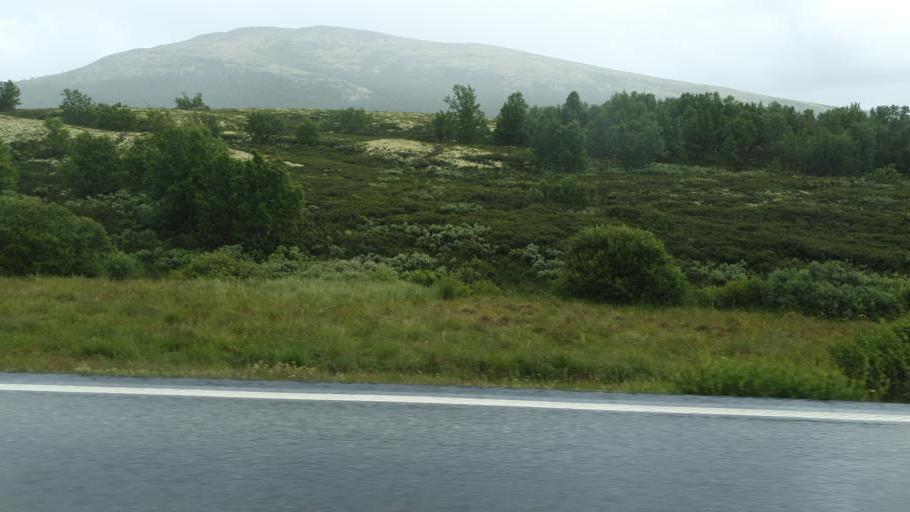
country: NO
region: Sor-Trondelag
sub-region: Oppdal
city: Oppdal
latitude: 62.2549
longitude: 9.5457
